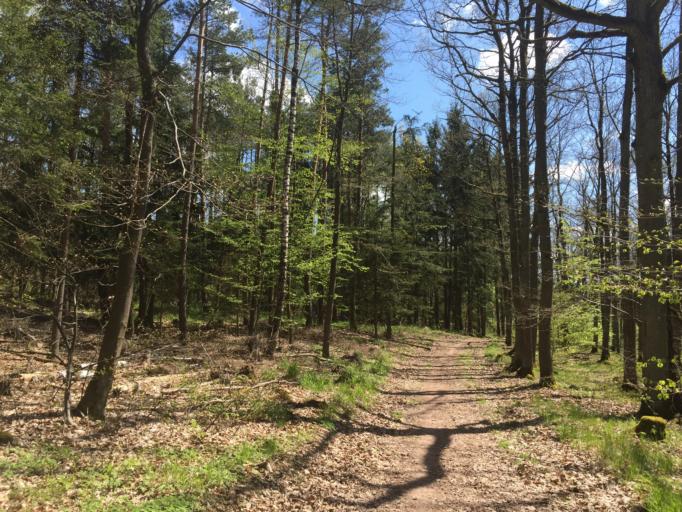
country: DE
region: Bavaria
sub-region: Regierungsbezirk Unterfranken
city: Sulzfeld
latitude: 50.2536
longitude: 10.4537
